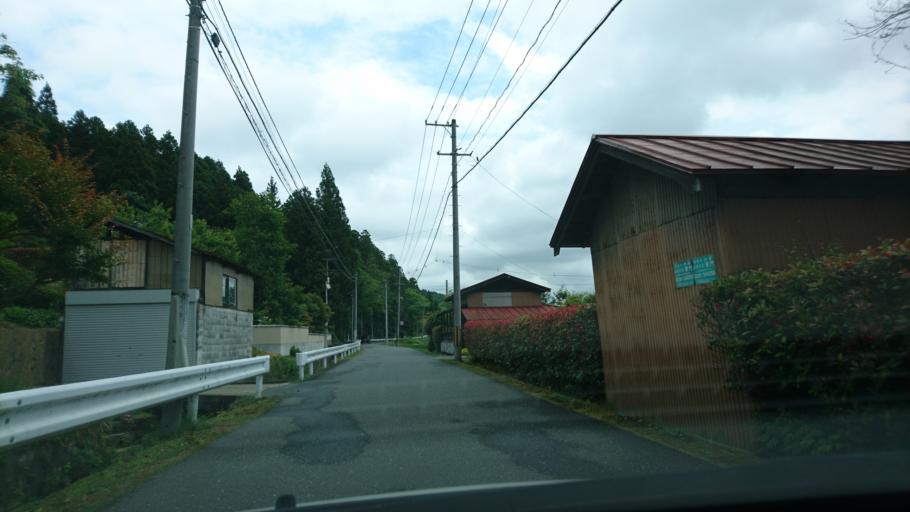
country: JP
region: Iwate
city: Ichinoseki
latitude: 38.9424
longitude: 141.0999
